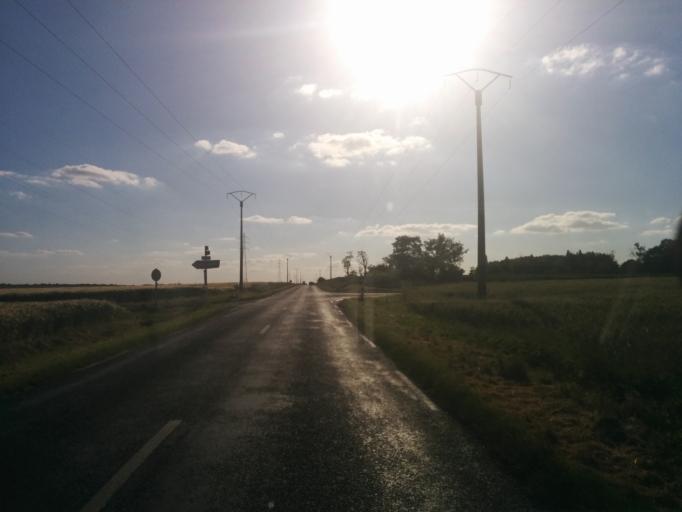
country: FR
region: Ile-de-France
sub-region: Departement des Yvelines
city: Limetz-Villez
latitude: 49.0945
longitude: 1.5607
